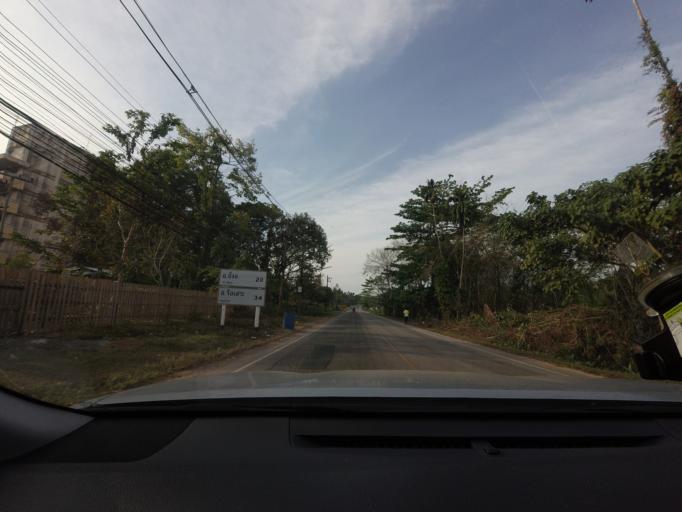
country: TH
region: Narathiwat
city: Ra-ngae
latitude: 6.2991
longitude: 101.7285
